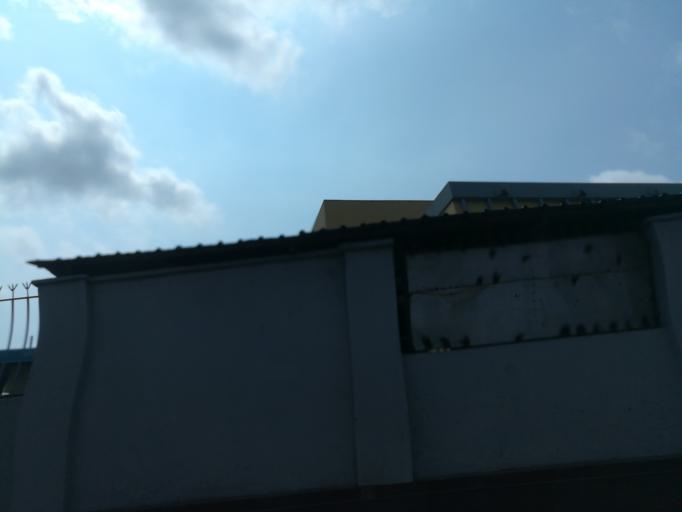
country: NG
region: Lagos
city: Lagos
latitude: 6.4491
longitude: 3.4023
